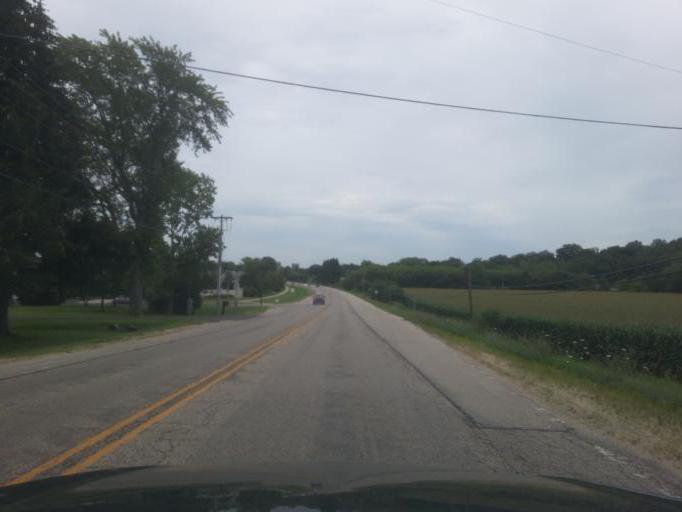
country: US
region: Wisconsin
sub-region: Dane County
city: Cottage Grove
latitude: 43.0850
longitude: -89.2619
